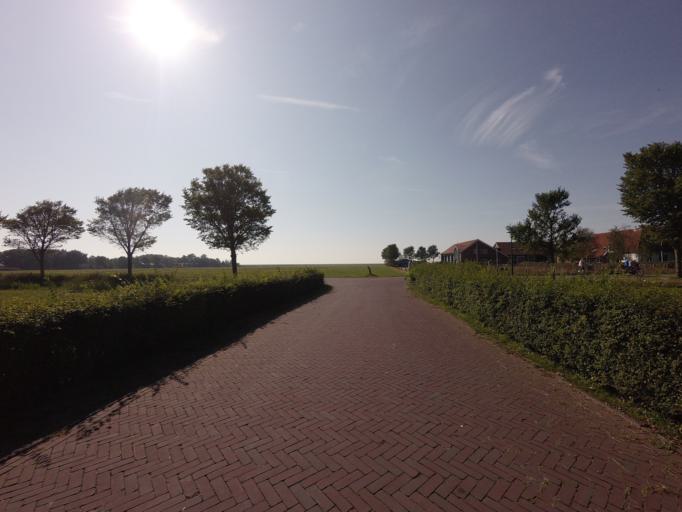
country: NL
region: Friesland
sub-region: Gemeente Schiermonnikoog
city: Schiermonnikoog
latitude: 53.4808
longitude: 6.1684
